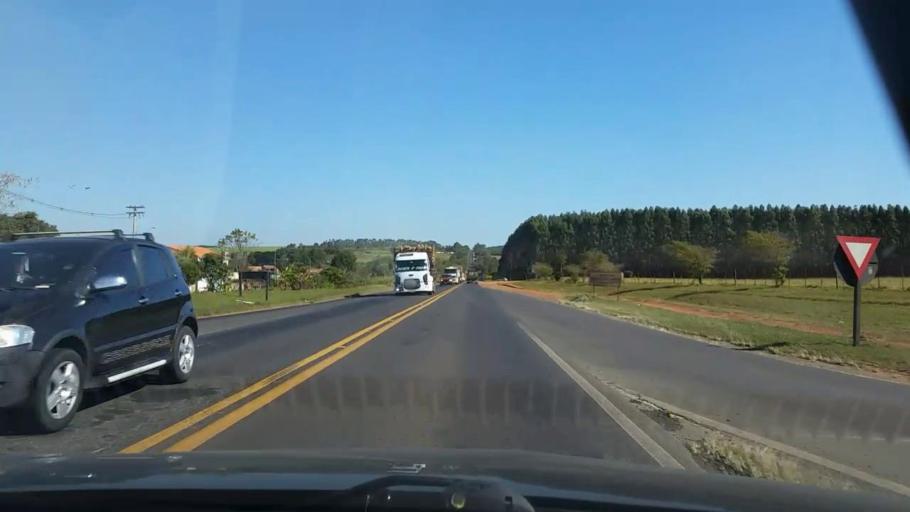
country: BR
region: Sao Paulo
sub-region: Sao Manuel
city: Sao Manuel
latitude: -22.8049
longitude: -48.6697
